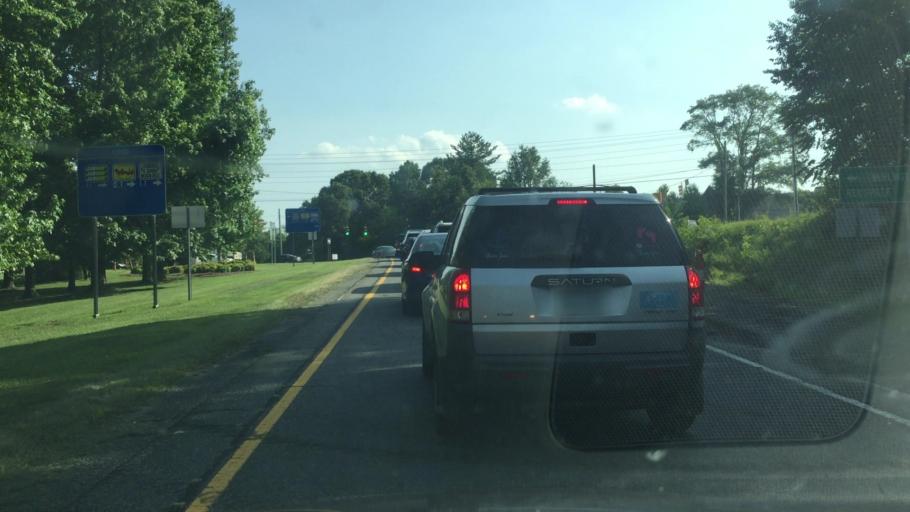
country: US
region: North Carolina
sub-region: Rockingham County
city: Reidsville
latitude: 36.3284
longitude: -79.6435
